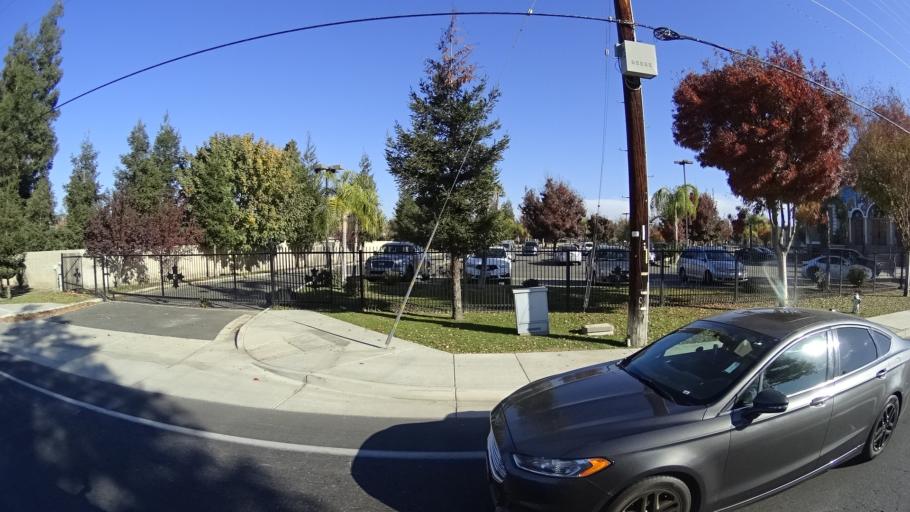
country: US
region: California
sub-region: Kern County
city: Greenacres
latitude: 35.3246
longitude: -119.1054
